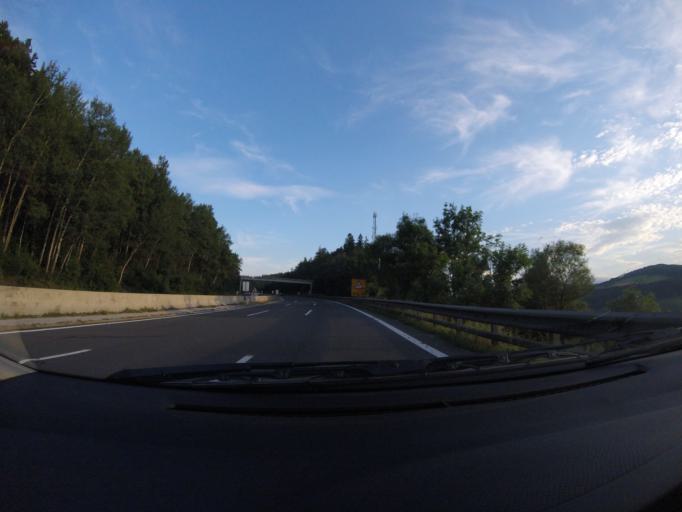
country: AT
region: Lower Austria
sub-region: Politischer Bezirk Neunkirchen
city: Edlitz
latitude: 47.5866
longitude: 16.1083
